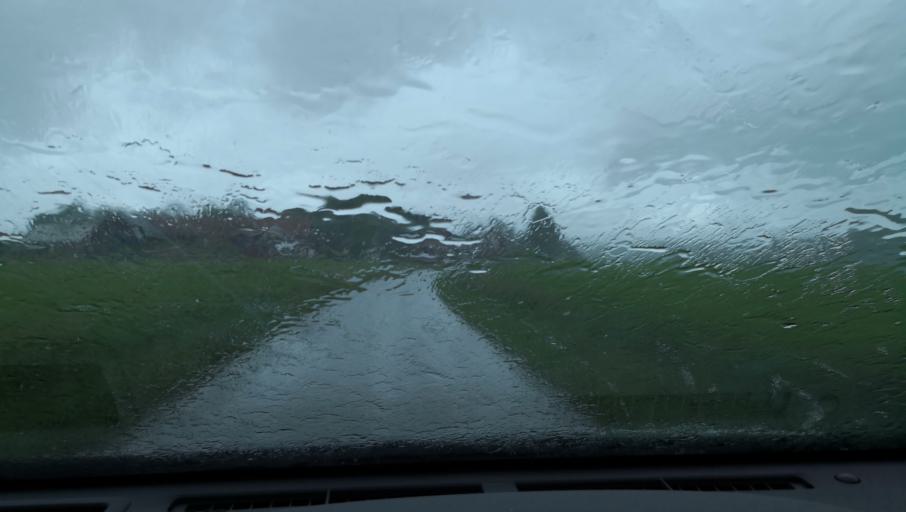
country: SE
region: Uppsala
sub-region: Enkopings Kommun
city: Orsundsbro
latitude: 59.7778
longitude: 17.3495
